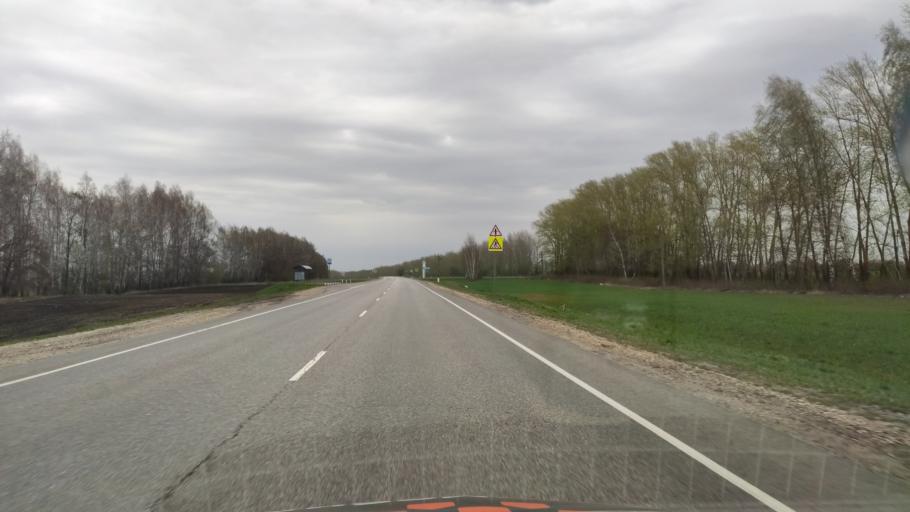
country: RU
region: Kursk
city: Olym
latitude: 51.5505
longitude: 38.1992
